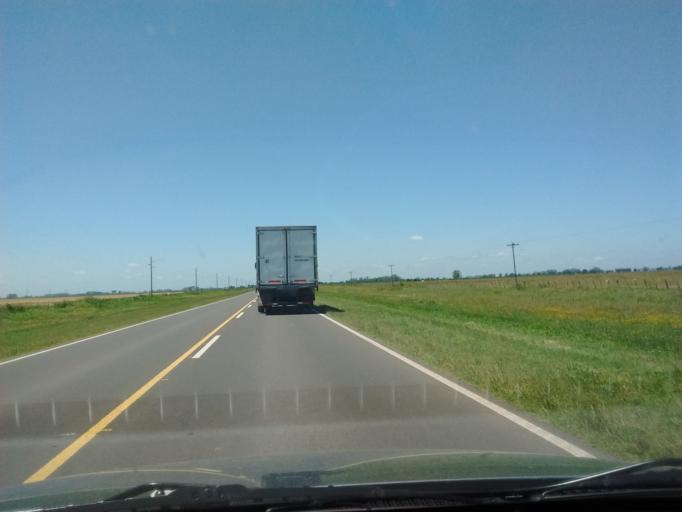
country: AR
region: Entre Rios
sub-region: Departamento de Gualeguay
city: Gualeguay
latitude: -33.0433
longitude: -59.4285
